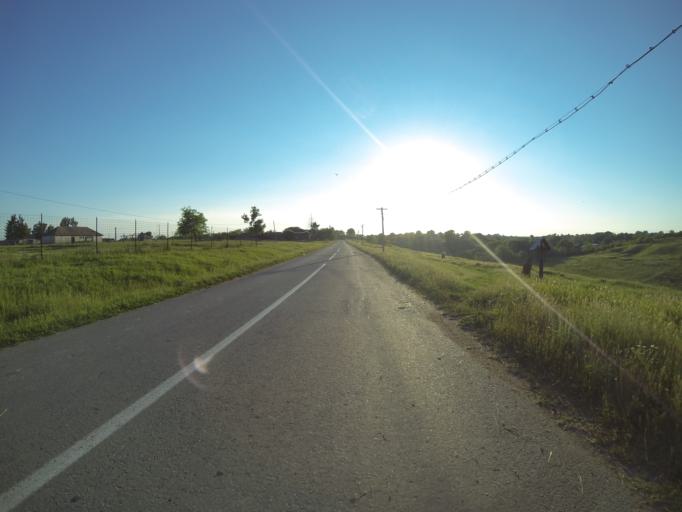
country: RO
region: Dolj
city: Satu Nou Calopar
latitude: 44.1621
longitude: 23.7695
